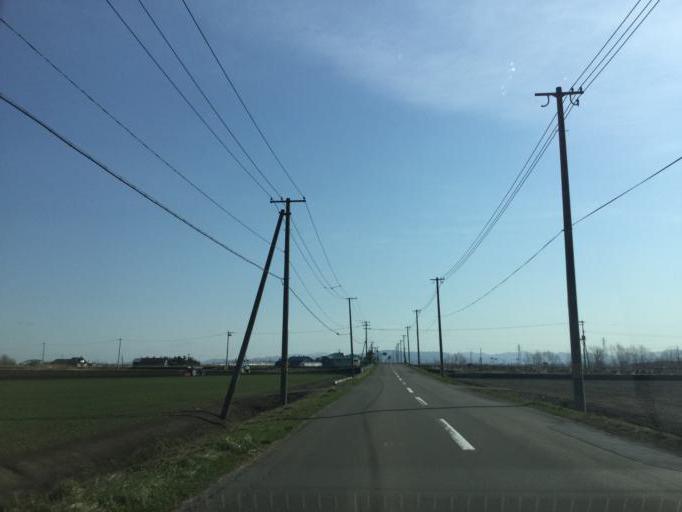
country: JP
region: Hokkaido
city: Iwamizawa
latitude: 43.1947
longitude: 141.7235
